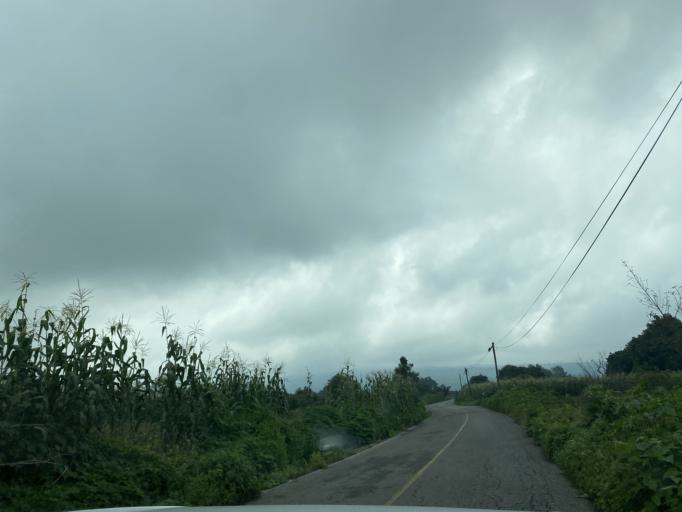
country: MX
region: Morelos
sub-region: Yecapixtla
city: Achichipico
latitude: 18.9359
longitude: -98.8131
